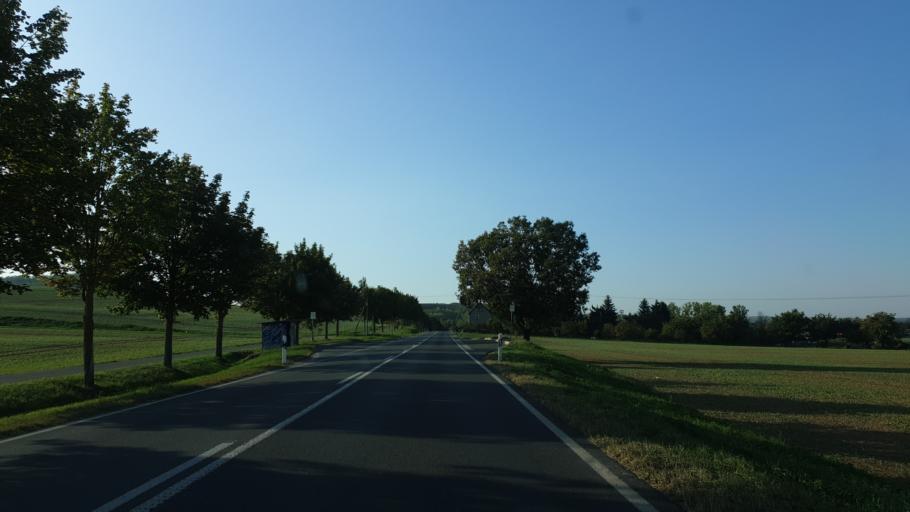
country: DE
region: Thuringia
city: Caaschwitz
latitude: 50.9397
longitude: 11.9962
